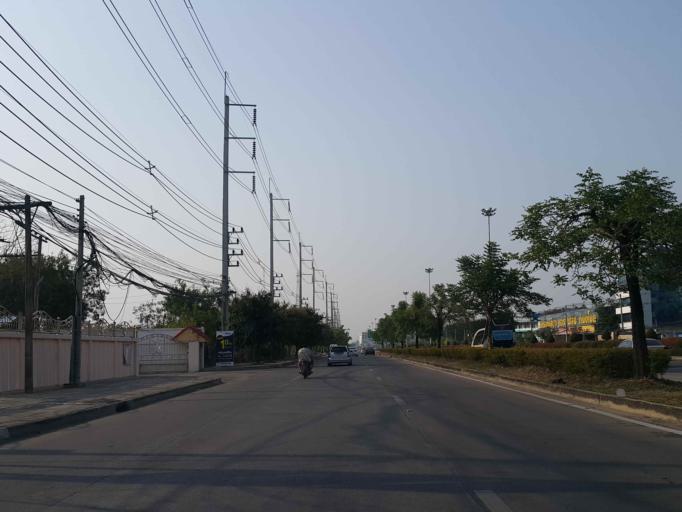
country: TH
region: Chiang Mai
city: Chiang Mai
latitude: 18.7693
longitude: 99.0285
